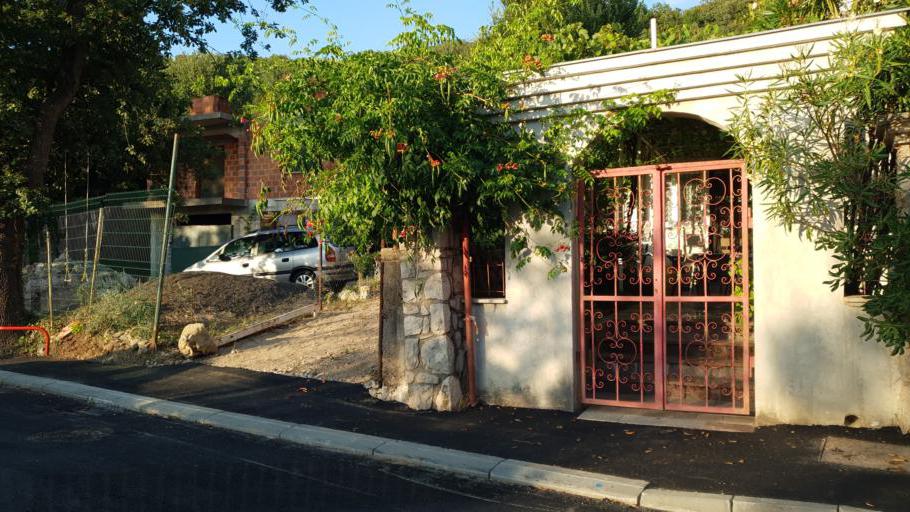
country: HR
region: Primorsko-Goranska
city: Omisalj
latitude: 45.2178
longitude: 14.5526
